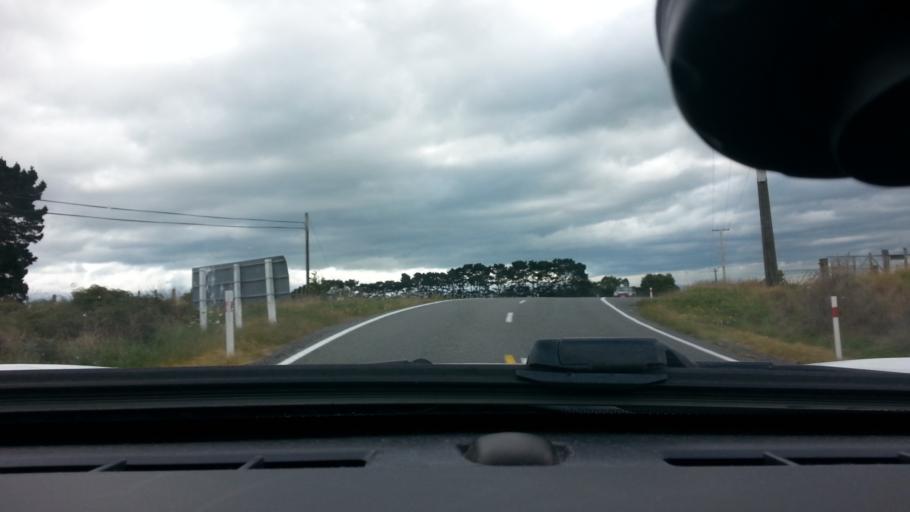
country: NZ
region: Wellington
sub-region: Upper Hutt City
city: Upper Hutt
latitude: -41.3614
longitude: 175.2000
